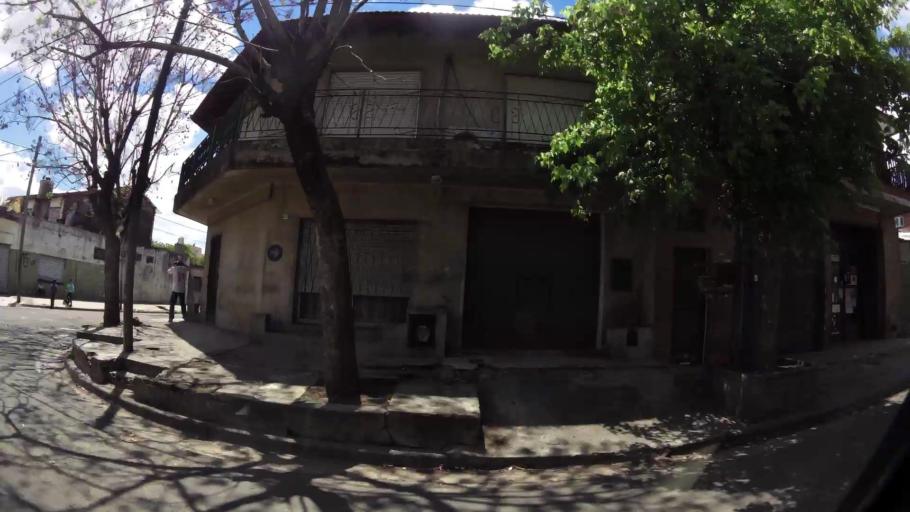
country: AR
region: Buenos Aires
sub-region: Partido de Lanus
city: Lanus
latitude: -34.6986
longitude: -58.4327
